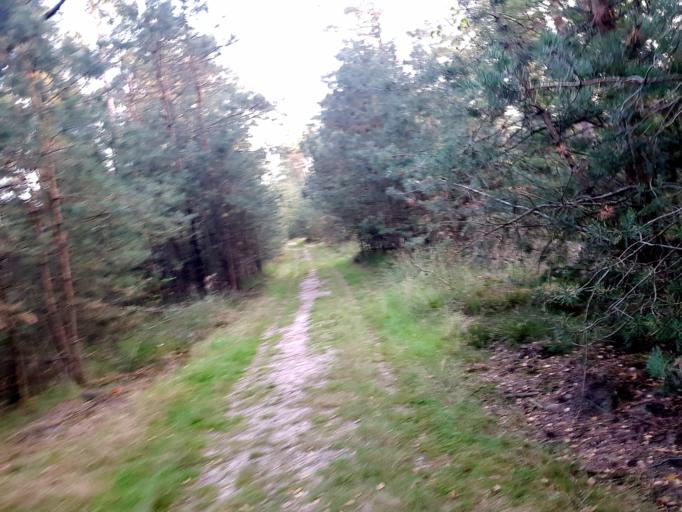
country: NL
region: Utrecht
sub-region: Gemeente Utrechtse Heuvelrug
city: Leersum
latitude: 52.0254
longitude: 5.4384
